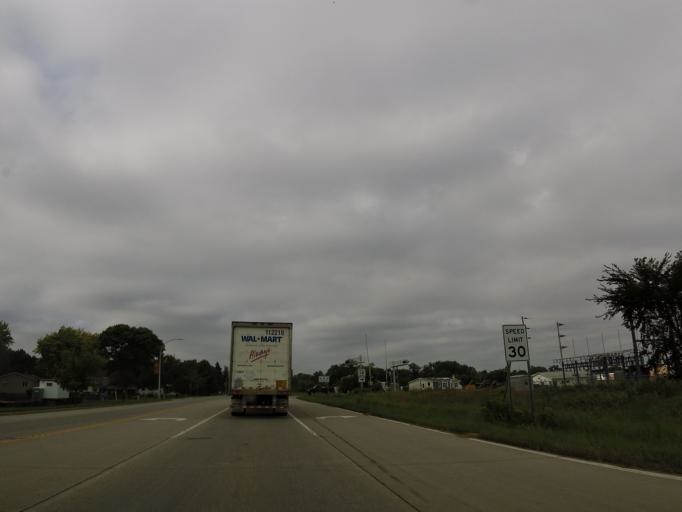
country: US
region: Minnesota
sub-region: Renville County
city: Olivia
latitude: 44.7761
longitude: -94.9750
